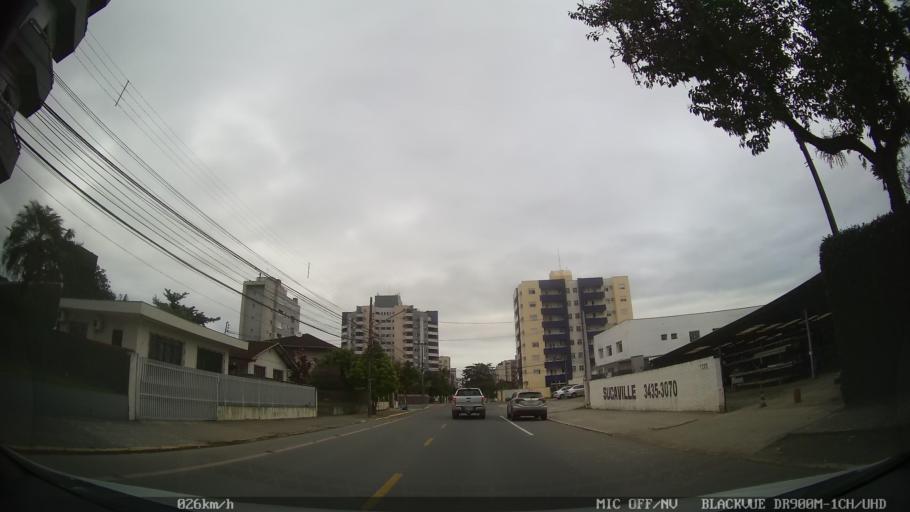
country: BR
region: Santa Catarina
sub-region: Joinville
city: Joinville
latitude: -26.2853
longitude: -48.8450
